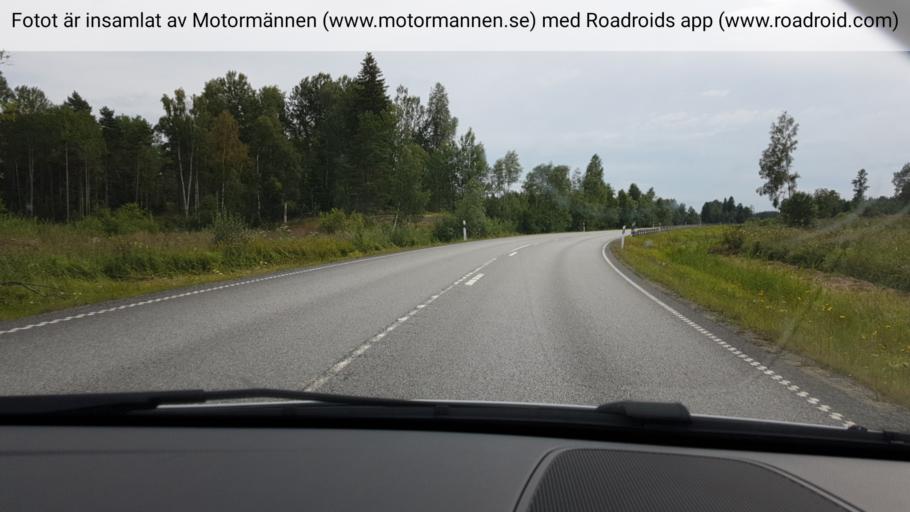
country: SE
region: Stockholm
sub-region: Norrtalje Kommun
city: Hallstavik
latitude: 60.0596
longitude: 18.5274
